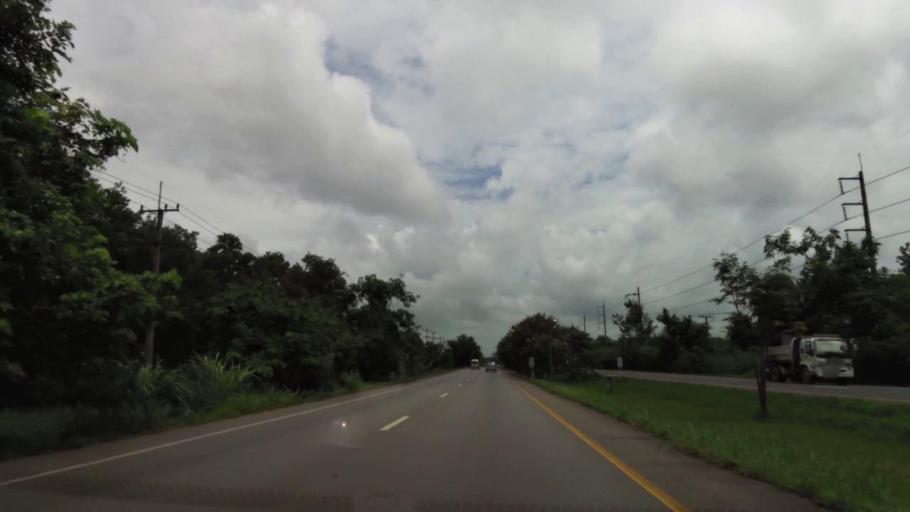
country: TH
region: Chanthaburi
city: Na Yai Am
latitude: 12.7485
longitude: 101.8762
